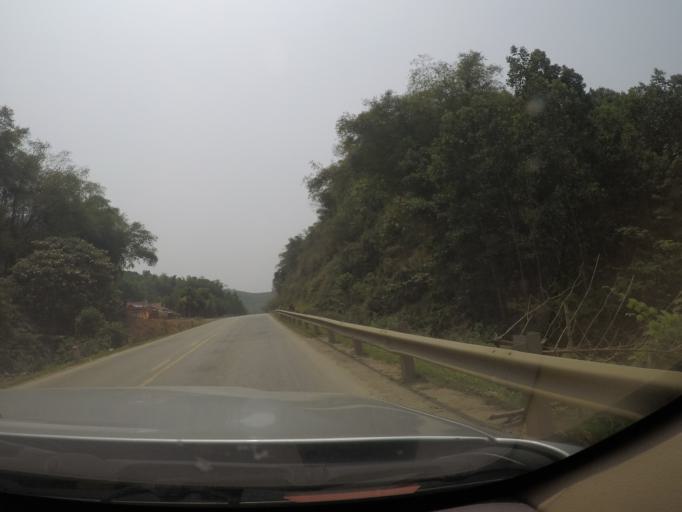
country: VN
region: Thanh Hoa
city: Thi Tran Thuong Xuan
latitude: 19.8390
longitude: 105.3994
